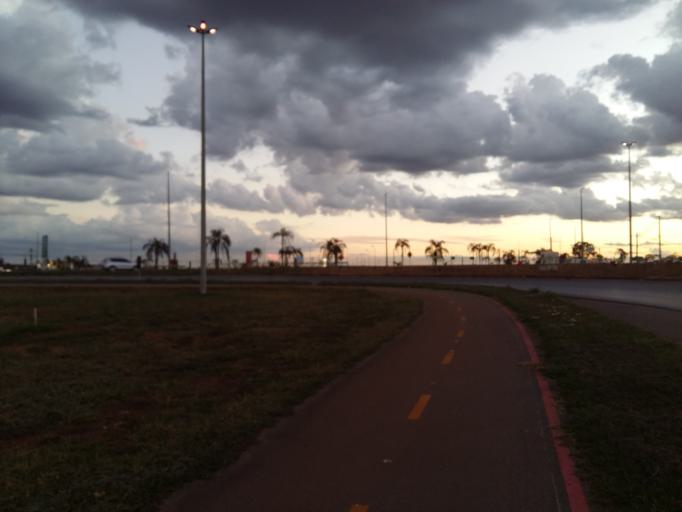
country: BR
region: Federal District
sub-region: Brasilia
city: Brasilia
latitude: -15.6867
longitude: -47.8579
